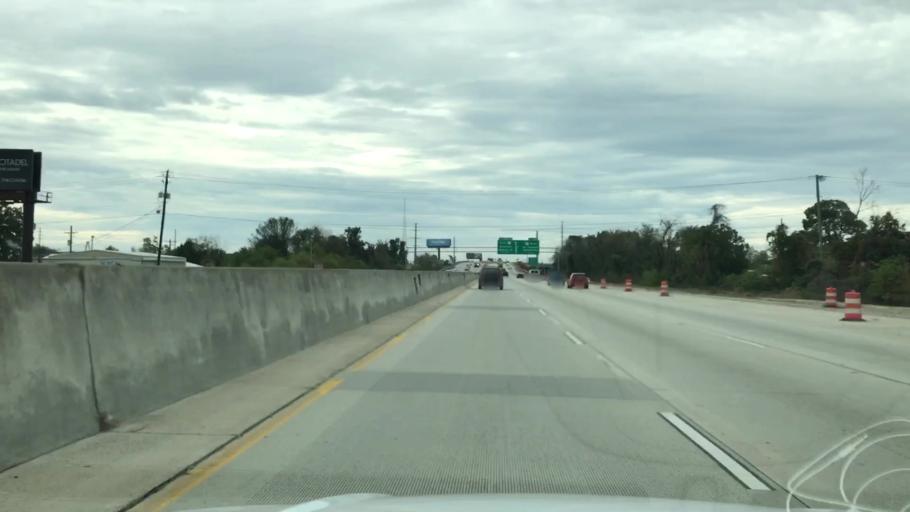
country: US
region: South Carolina
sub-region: Charleston County
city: North Charleston
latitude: 32.8305
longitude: -79.9559
